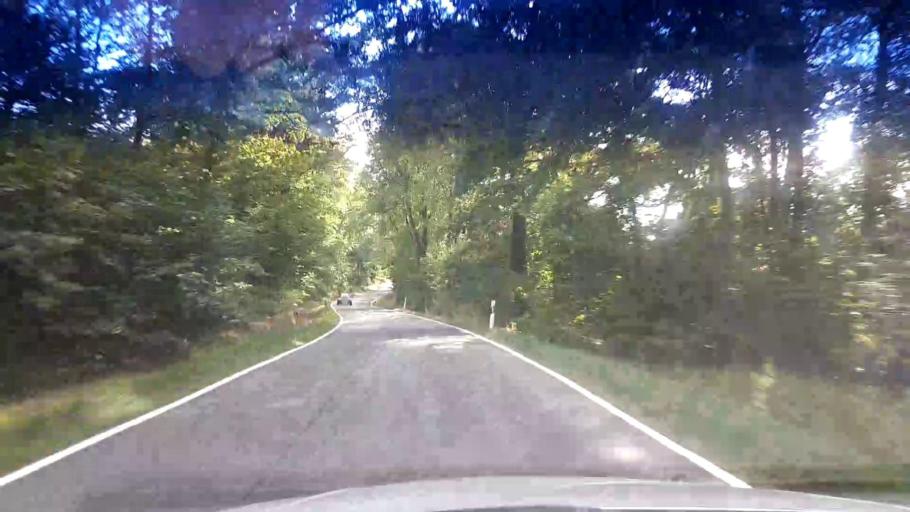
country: DE
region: Bavaria
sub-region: Upper Palatinate
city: Tirschenreuth
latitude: 49.9118
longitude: 12.3901
